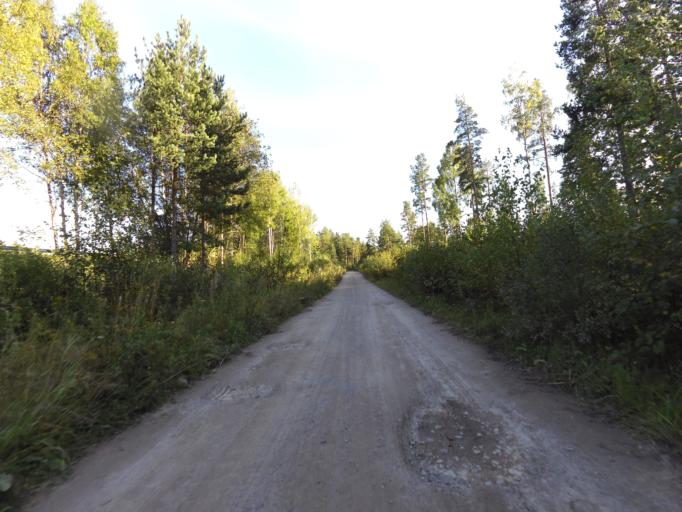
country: SE
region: Gaevleborg
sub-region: Gavle Kommun
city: Gavle
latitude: 60.6522
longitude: 17.1152
